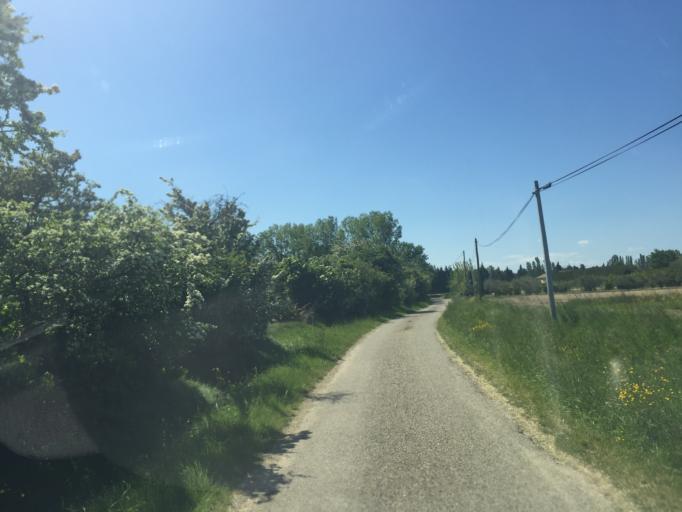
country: FR
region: Provence-Alpes-Cote d'Azur
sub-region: Departement du Vaucluse
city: Orange
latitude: 44.1397
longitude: 4.7858
